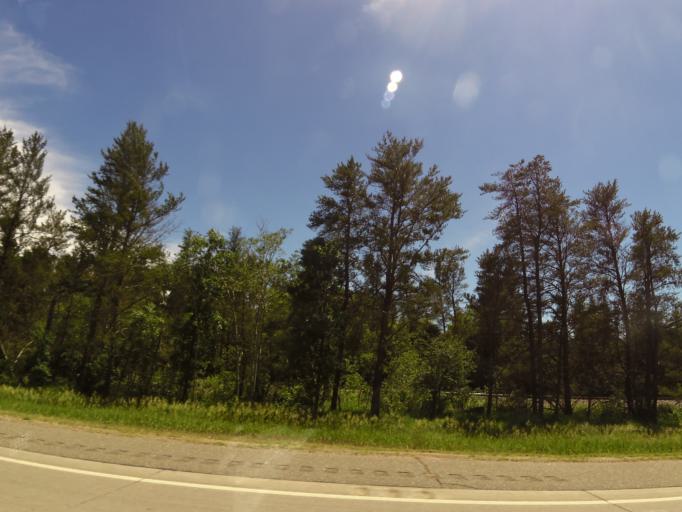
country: US
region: Minnesota
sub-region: Todd County
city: Staples
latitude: 46.3423
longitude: -94.6838
